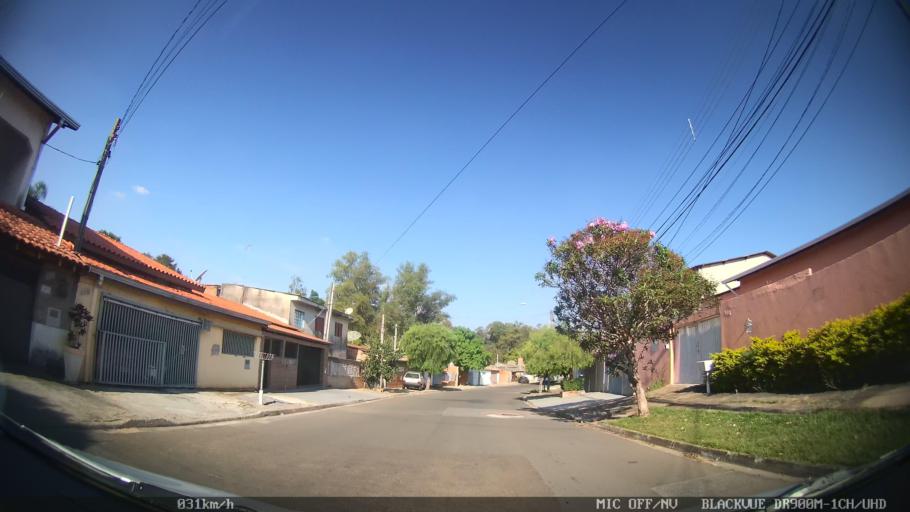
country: BR
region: Sao Paulo
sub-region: Campinas
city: Campinas
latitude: -22.9938
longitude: -47.1384
